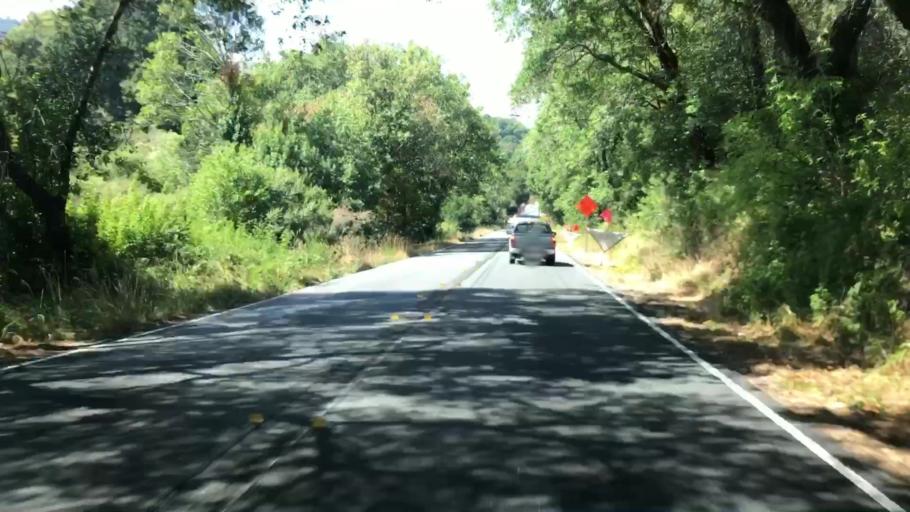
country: US
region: California
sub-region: Marin County
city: Lagunitas-Forest Knolls
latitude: 37.9935
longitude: -122.7530
